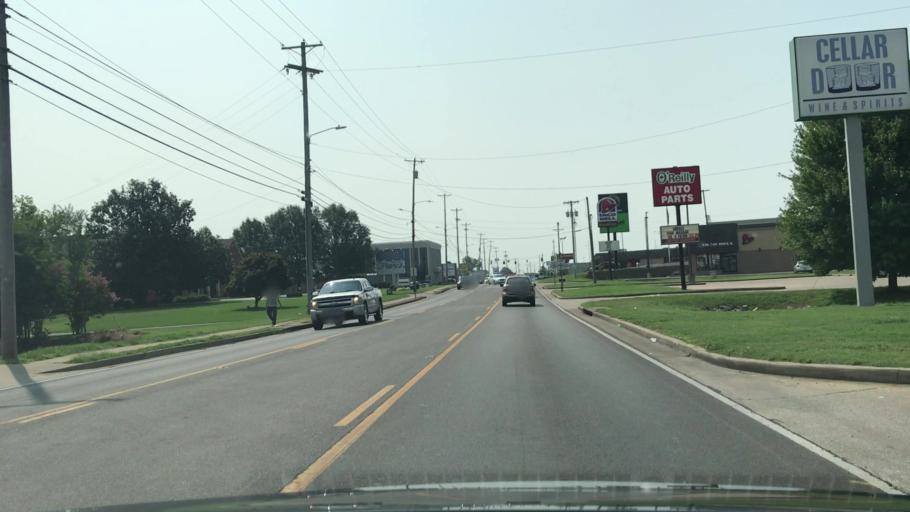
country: US
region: Kentucky
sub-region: Graves County
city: Mayfield
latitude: 36.7273
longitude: -88.6301
